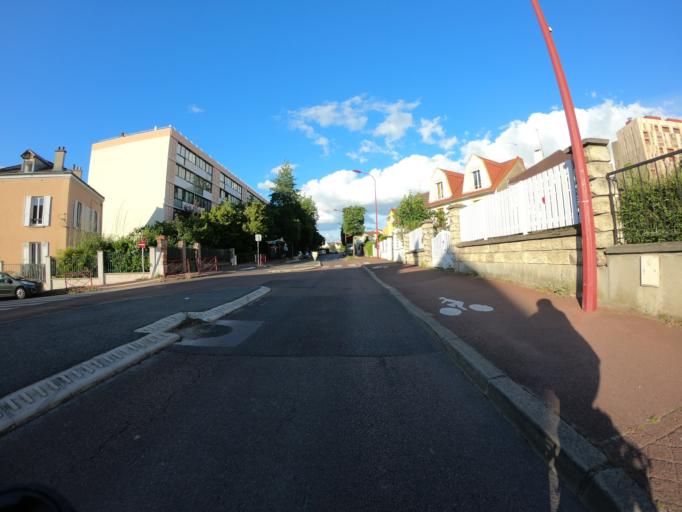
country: FR
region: Ile-de-France
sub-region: Departement du Val-de-Marne
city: Fresnes
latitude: 48.7547
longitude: 2.3170
